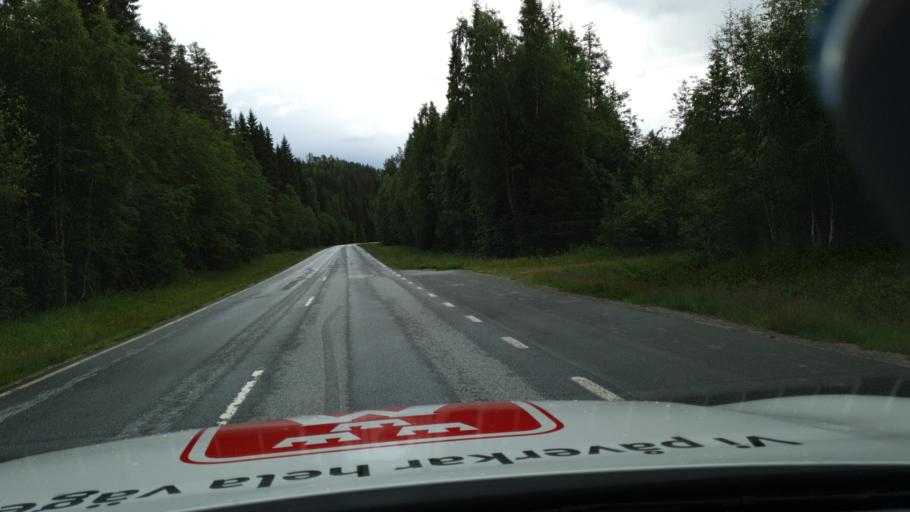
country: SE
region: Vaesterbotten
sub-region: Dorotea Kommun
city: Dorotea
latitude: 63.8676
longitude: 16.3821
